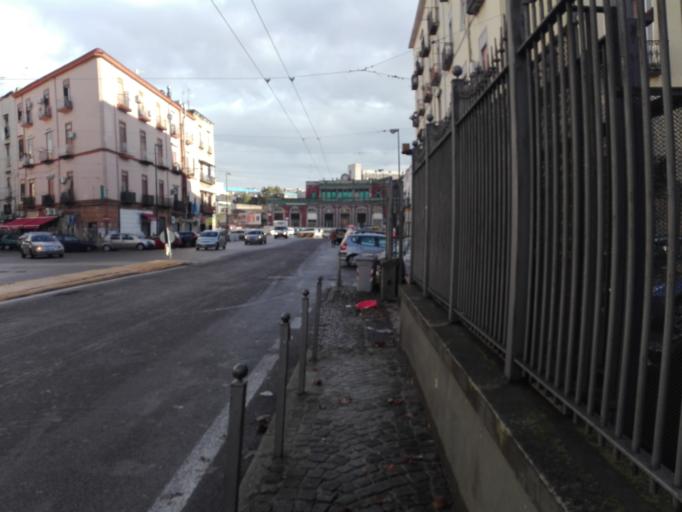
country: IT
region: Campania
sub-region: Provincia di Napoli
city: Napoli
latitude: 40.8648
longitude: 14.2684
